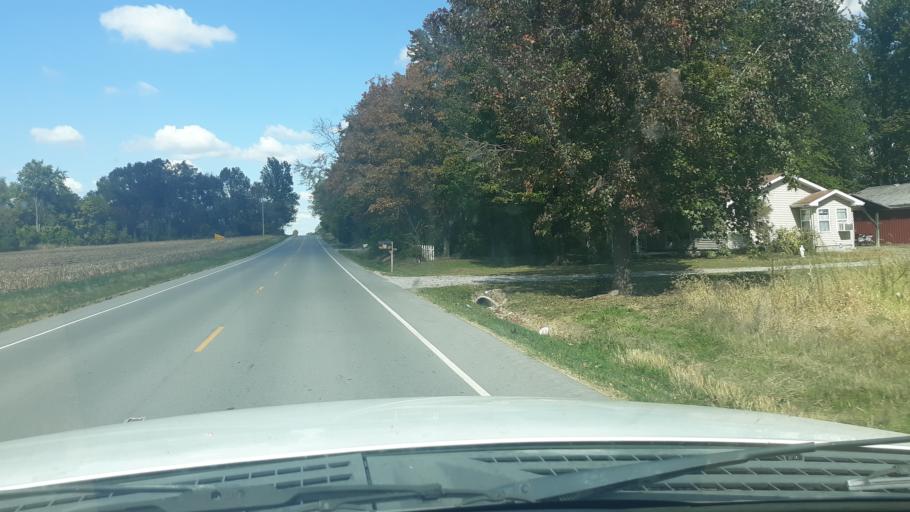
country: US
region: Illinois
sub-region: Saline County
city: Eldorado
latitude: 37.8134
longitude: -88.4848
